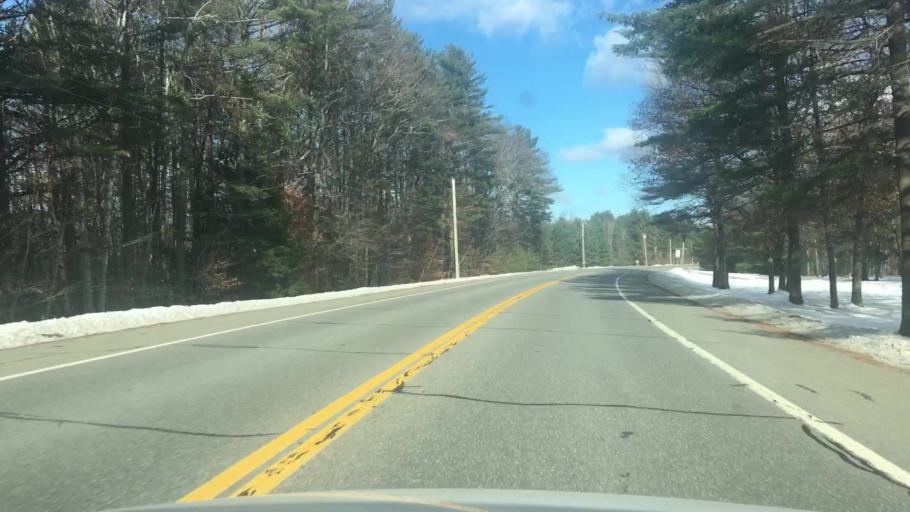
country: US
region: Maine
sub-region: Somerset County
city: Madison
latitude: 44.9822
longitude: -69.8675
